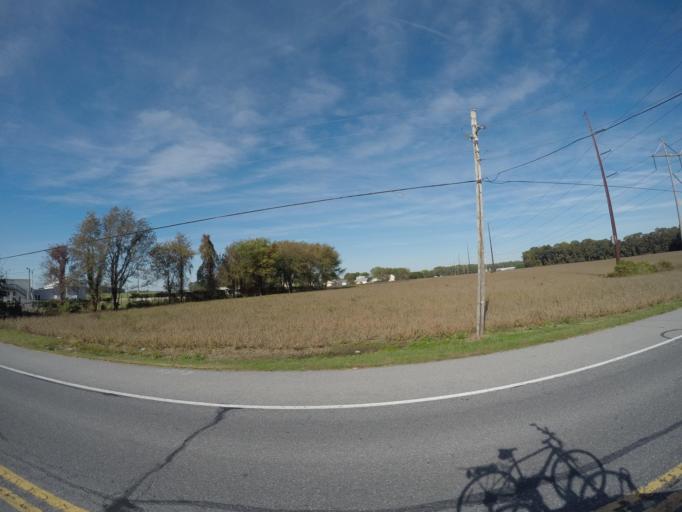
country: US
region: Delaware
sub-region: Sussex County
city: Milton
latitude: 38.7960
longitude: -75.2862
